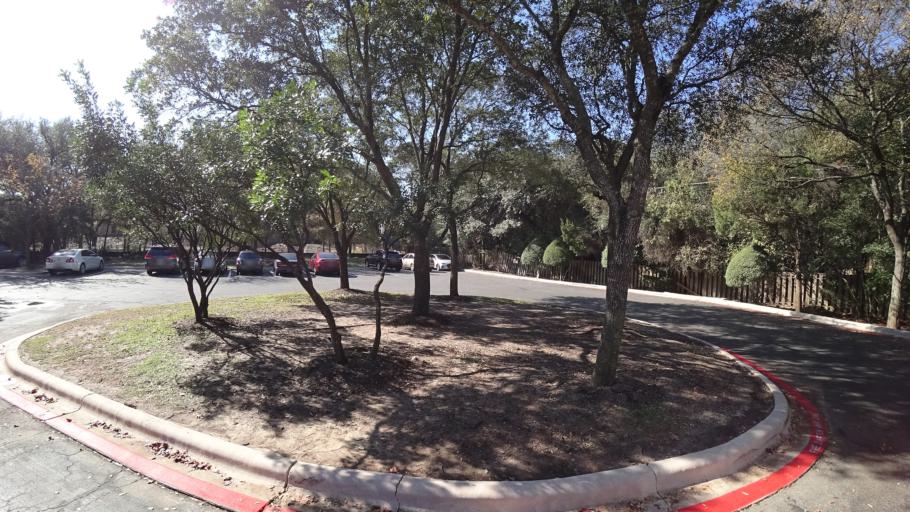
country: US
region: Texas
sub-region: Williamson County
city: Jollyville
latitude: 30.3717
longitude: -97.7595
